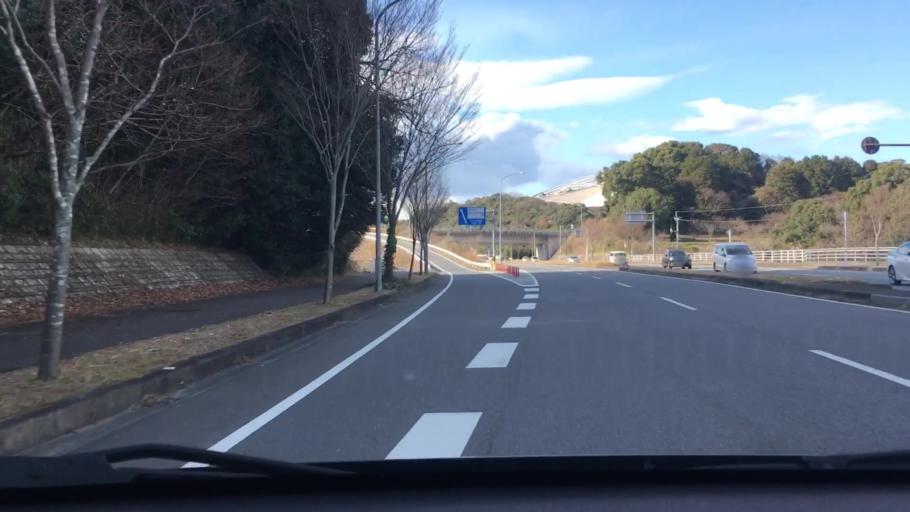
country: JP
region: Oita
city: Tsurusaki
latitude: 33.1944
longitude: 131.6652
